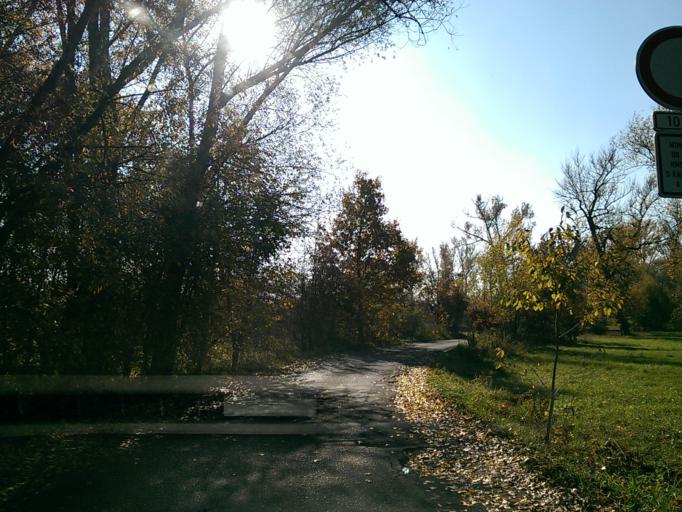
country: CZ
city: Prisovice
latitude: 50.5654
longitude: 15.0856
